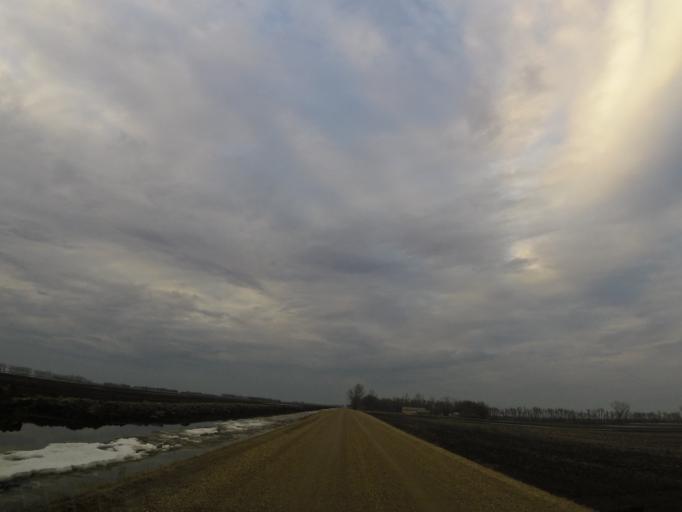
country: US
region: North Dakota
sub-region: Walsh County
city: Grafton
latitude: 48.3835
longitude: -97.2119
